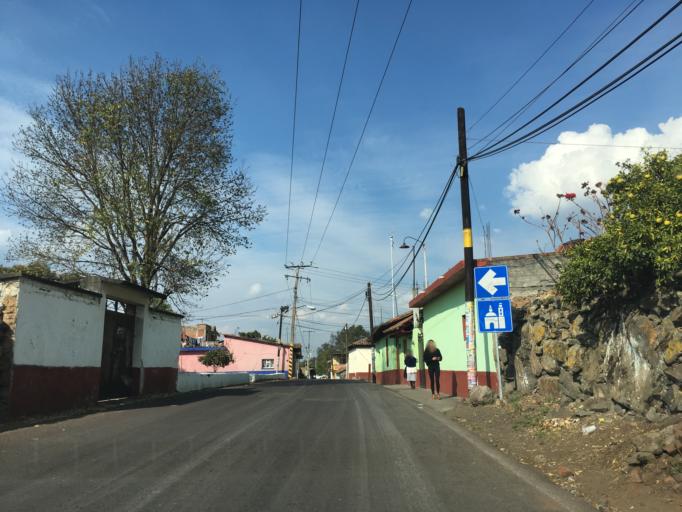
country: MX
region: Michoacan
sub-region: Patzcuaro
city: Santa Ana Chapitiro
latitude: 19.5382
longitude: -101.6329
